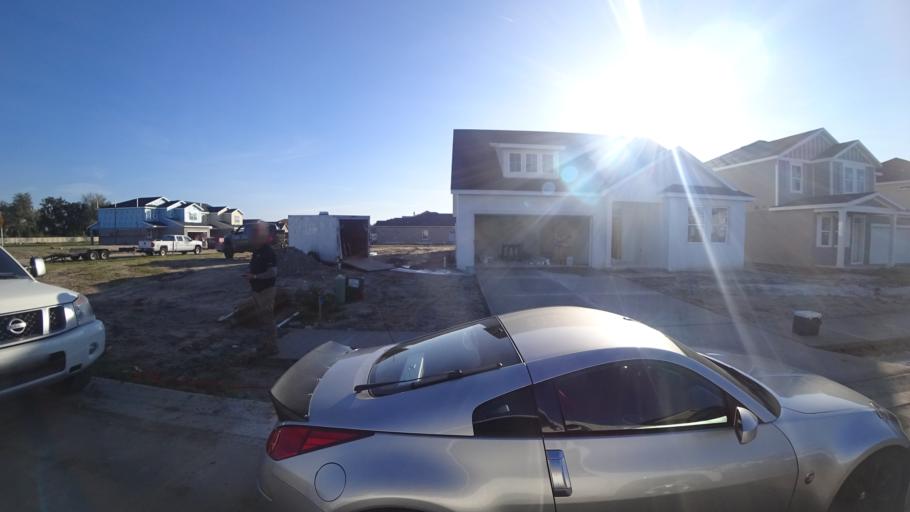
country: US
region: Florida
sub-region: Manatee County
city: Ellenton
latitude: 27.5561
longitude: -82.5223
